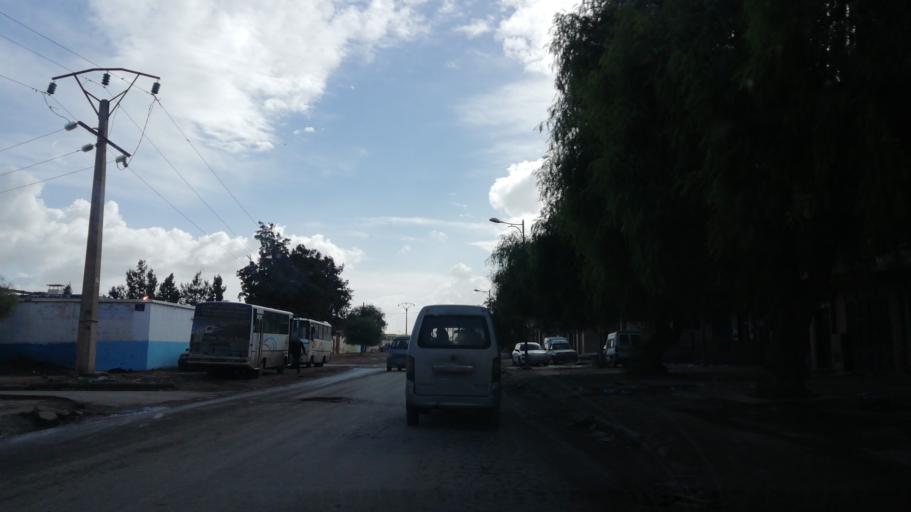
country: DZ
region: Oran
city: Sidi ech Chahmi
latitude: 35.6507
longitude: -0.5654
